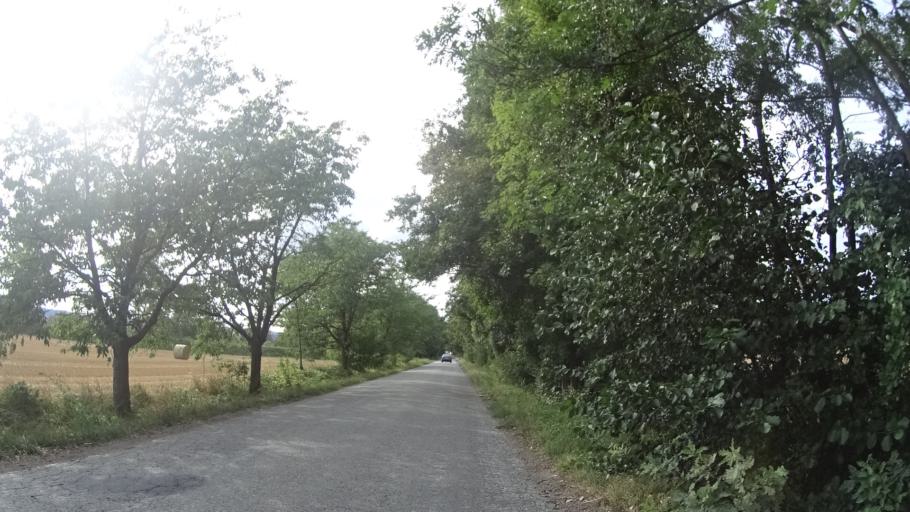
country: CZ
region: Olomoucky
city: Dubicko
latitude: 49.8016
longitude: 16.9475
